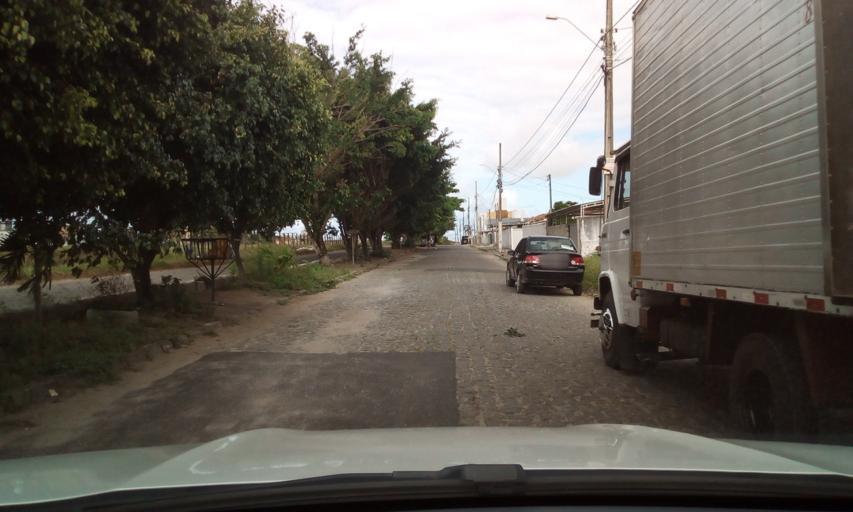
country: BR
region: Paraiba
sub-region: Joao Pessoa
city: Joao Pessoa
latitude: -7.1861
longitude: -34.8762
